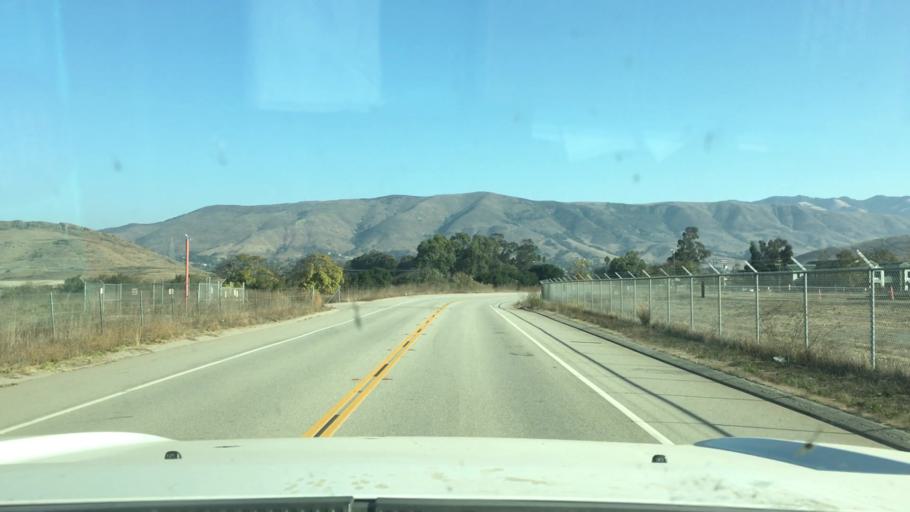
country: US
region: California
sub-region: San Luis Obispo County
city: San Luis Obispo
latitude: 35.2430
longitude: -120.6518
